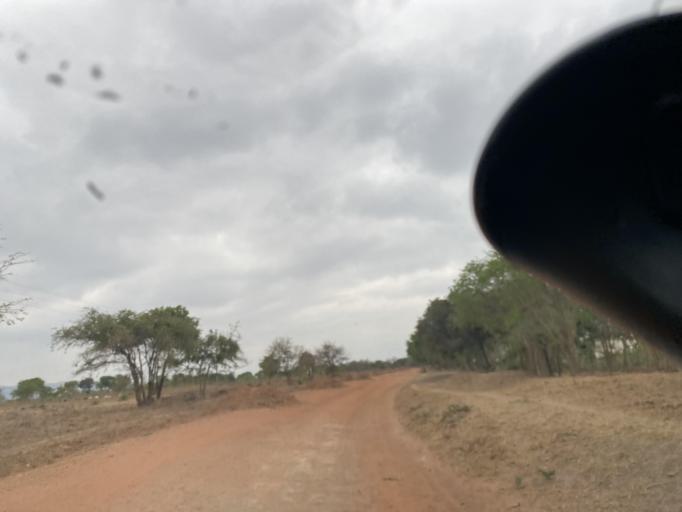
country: ZM
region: Lusaka
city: Chongwe
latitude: -15.2238
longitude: 28.7475
